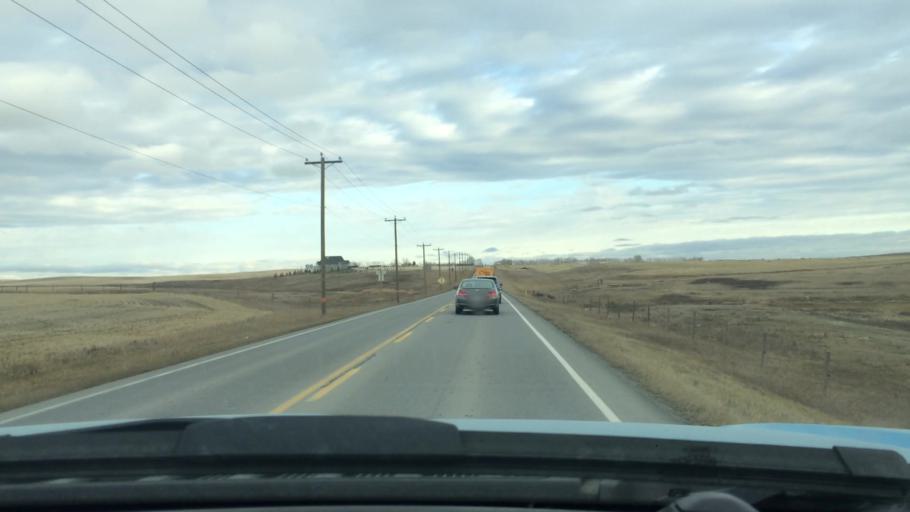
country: CA
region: Alberta
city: Airdrie
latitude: 51.2145
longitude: -114.0249
